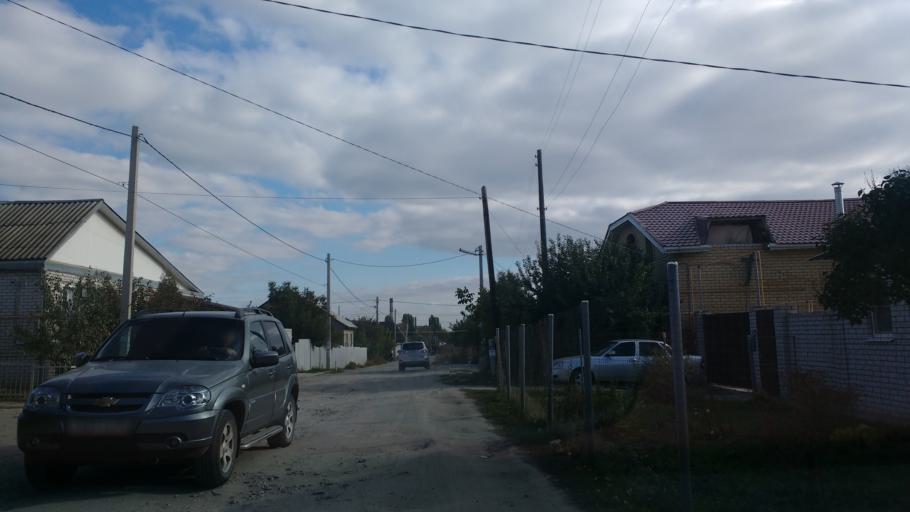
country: RU
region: Volgograd
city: Volgograd
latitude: 48.7574
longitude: 44.5416
